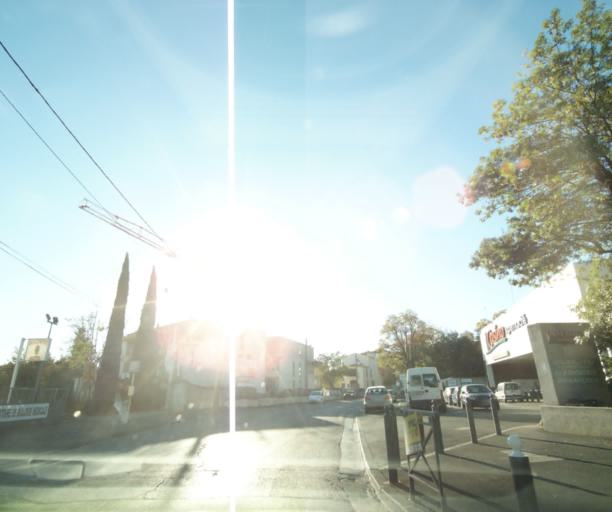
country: FR
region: Provence-Alpes-Cote d'Azur
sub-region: Departement des Bouches-du-Rhone
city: Marseille 13
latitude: 43.3254
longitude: 5.4190
